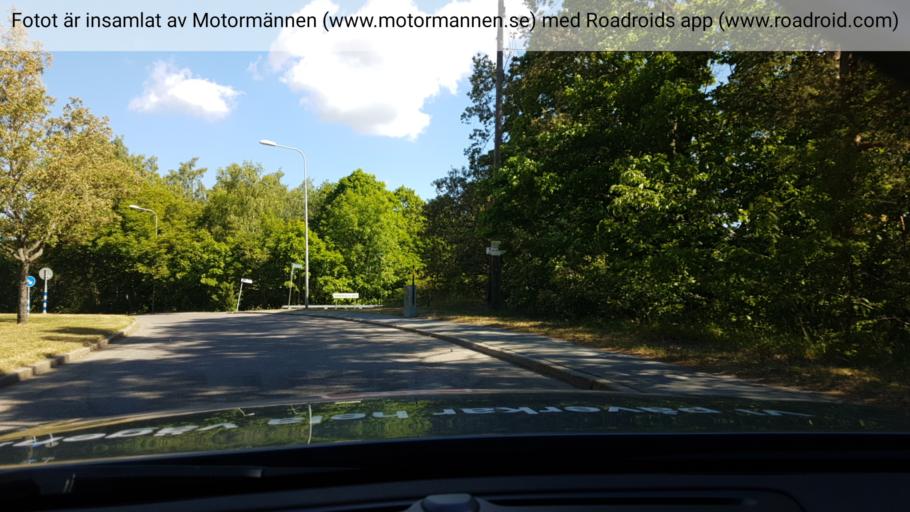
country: SE
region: Stockholm
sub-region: Stockholms Kommun
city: Arsta
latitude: 59.2486
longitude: 18.1055
